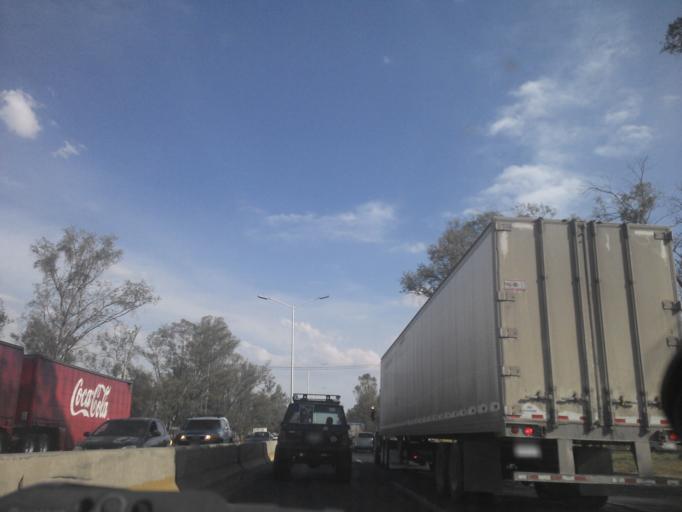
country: MX
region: Jalisco
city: Guadalajara
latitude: 20.6559
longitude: -103.4465
